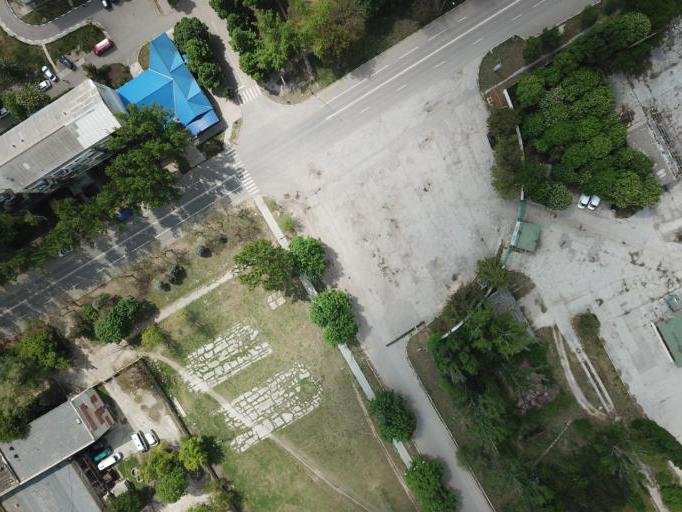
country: MD
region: Ungheni
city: Ungheni
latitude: 47.2217
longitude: 27.7986
